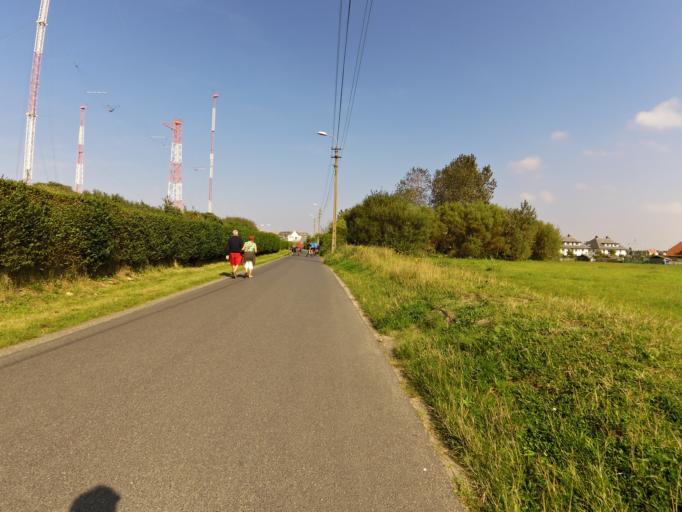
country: BE
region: Flanders
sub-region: Provincie West-Vlaanderen
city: Middelkerke
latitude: 51.1813
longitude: 2.8073
